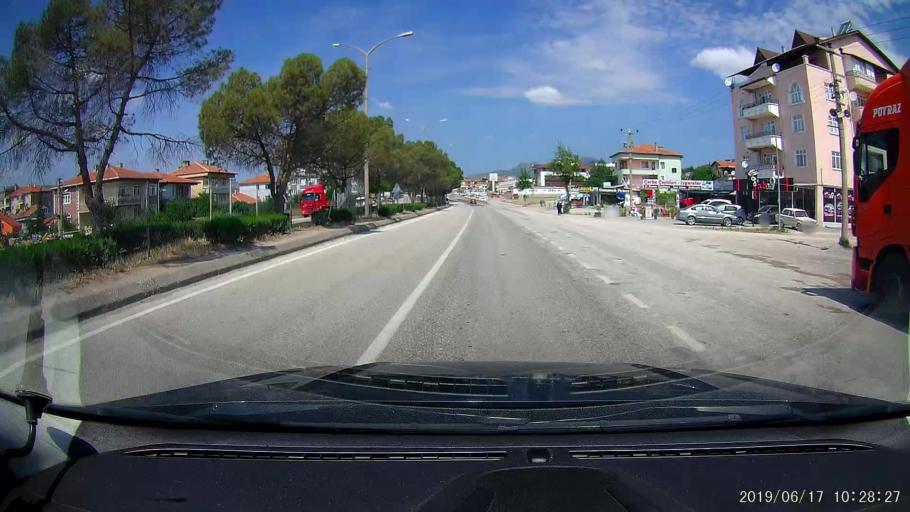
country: TR
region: Corum
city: Osmancik
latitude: 40.9782
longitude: 34.8078
